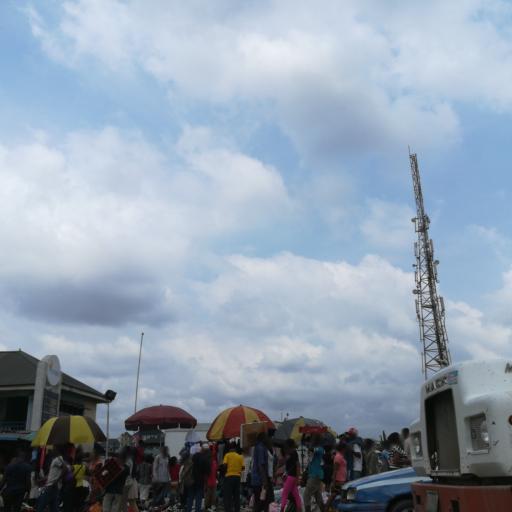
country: NG
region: Rivers
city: Port Harcourt
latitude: 4.8539
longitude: 7.0638
